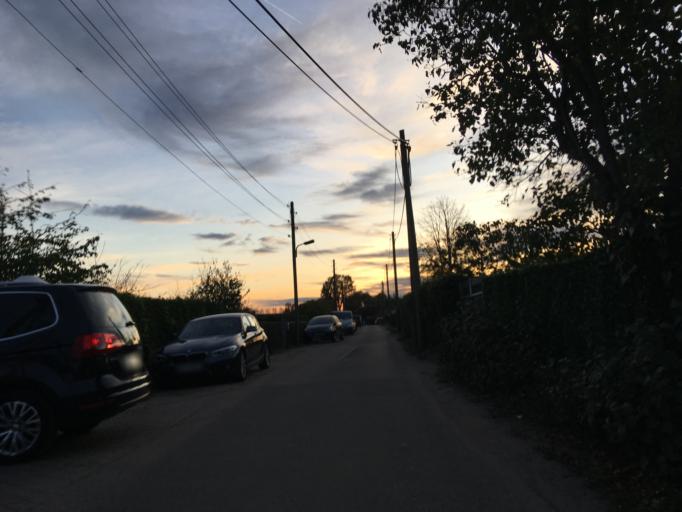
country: DE
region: Berlin
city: Buchholz
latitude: 52.6171
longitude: 13.4157
